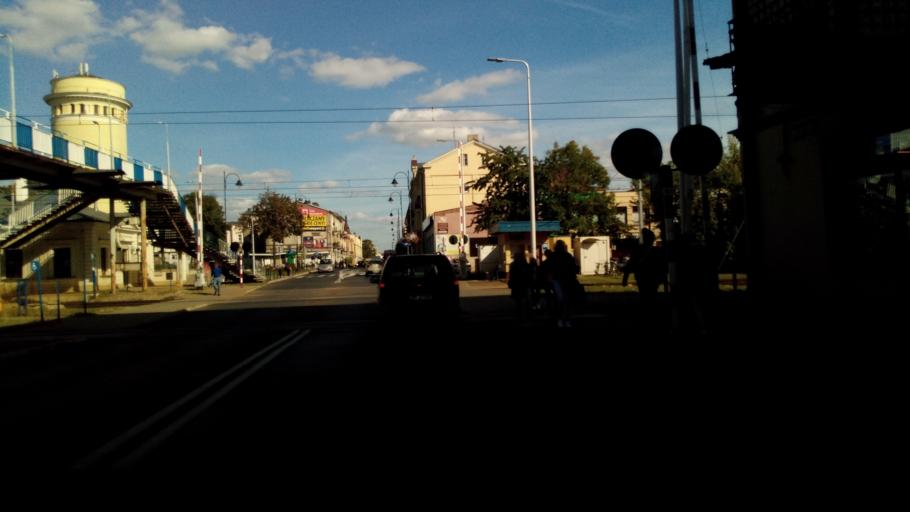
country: PL
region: Lodz Voivodeship
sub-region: Piotrkow Trybunalski
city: Piotrkow Trybunalski
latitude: 51.4092
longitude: 19.6840
